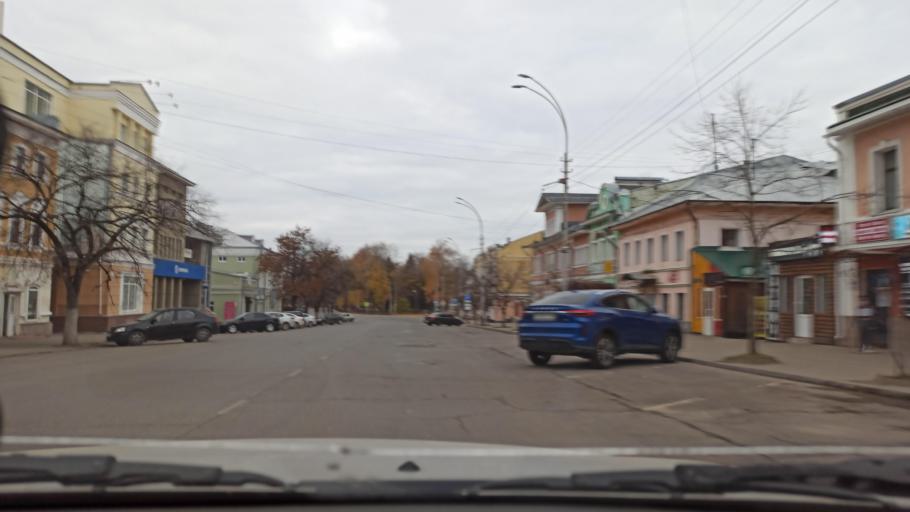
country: RU
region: Vologda
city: Vologda
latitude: 59.2210
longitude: 39.8940
